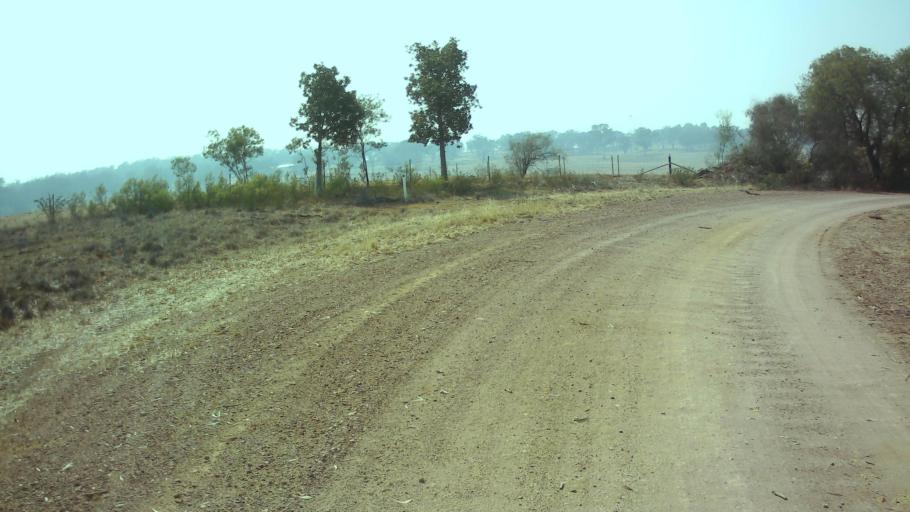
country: AU
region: New South Wales
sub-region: Weddin
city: Grenfell
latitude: -33.9043
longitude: 148.1728
